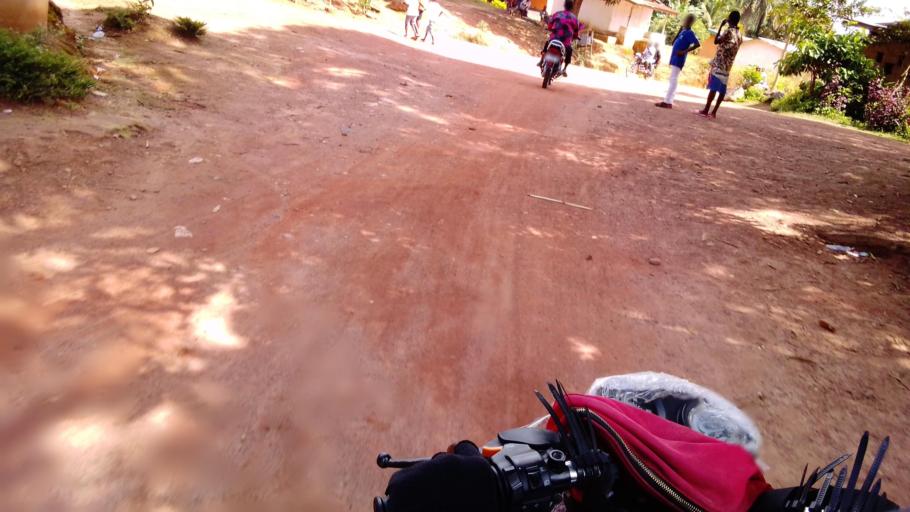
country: SL
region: Eastern Province
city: Koidu
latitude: 8.6611
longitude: -10.9759
